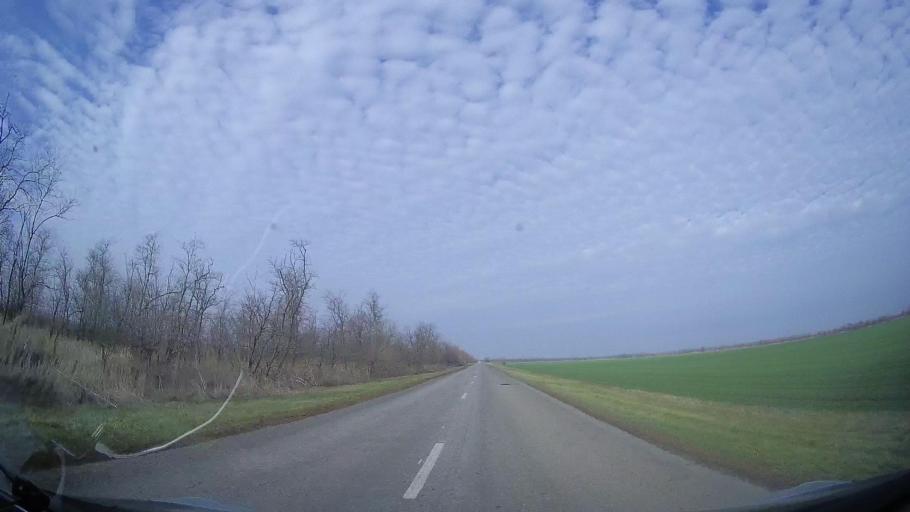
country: RU
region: Rostov
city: Gigant
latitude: 46.8676
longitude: 41.2763
